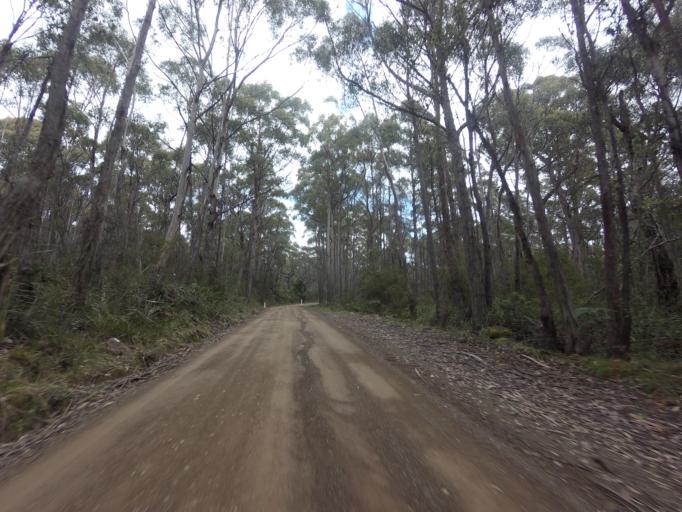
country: AU
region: Tasmania
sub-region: Huon Valley
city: Geeveston
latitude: -43.4248
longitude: 147.0064
